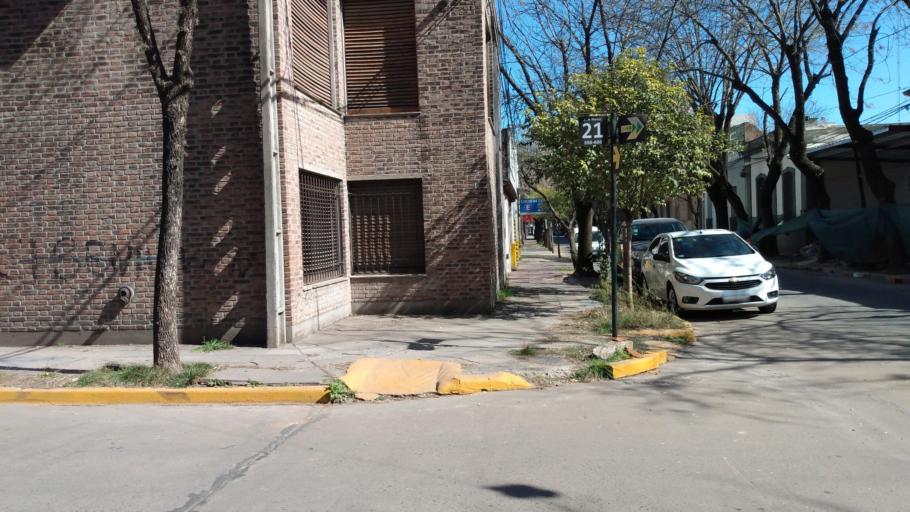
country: AR
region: Buenos Aires
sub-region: Partido de Mercedes
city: Mercedes
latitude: -34.6510
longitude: -59.4283
